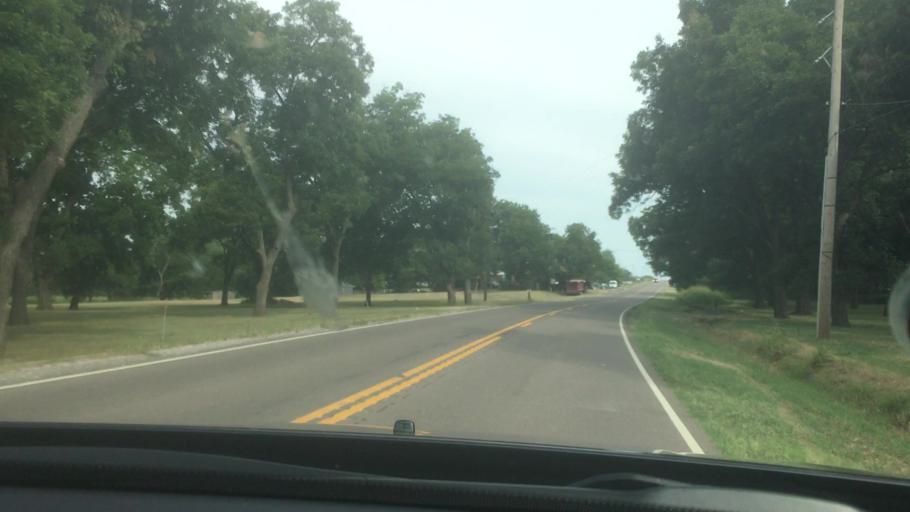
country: US
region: Oklahoma
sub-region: Garvin County
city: Pauls Valley
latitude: 34.7417
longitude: -97.2785
